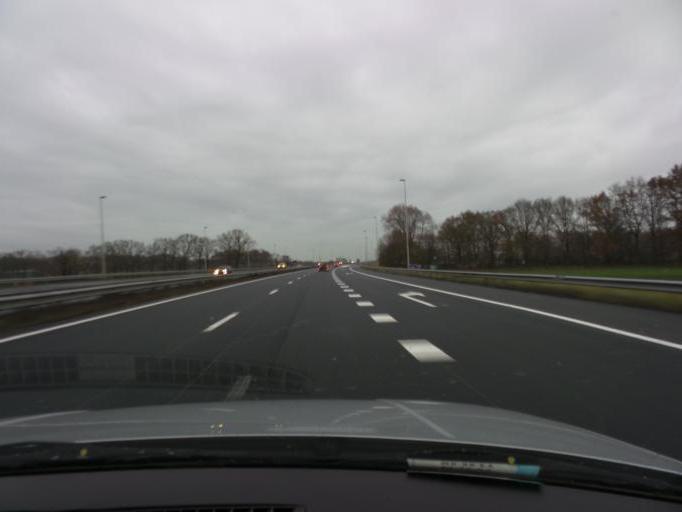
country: NL
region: Gelderland
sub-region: Gemeente Hattem
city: Hattem
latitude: 52.4634
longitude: 5.9838
